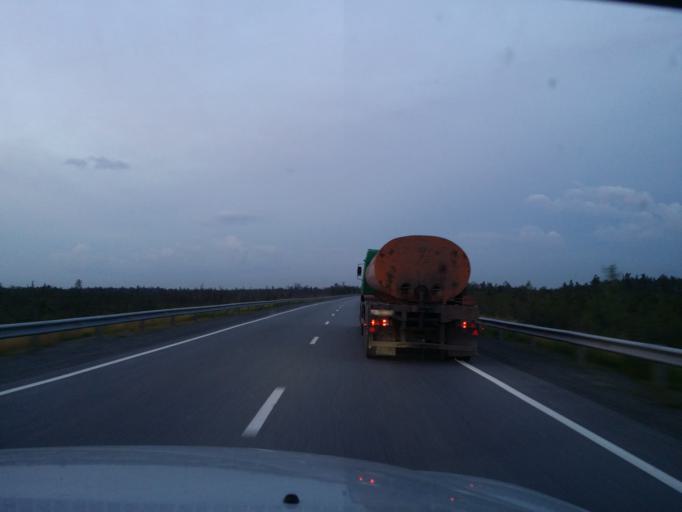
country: RU
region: Khanty-Mansiyskiy Avtonomnyy Okrug
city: Poykovskiy
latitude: 61.3555
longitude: 73.3036
